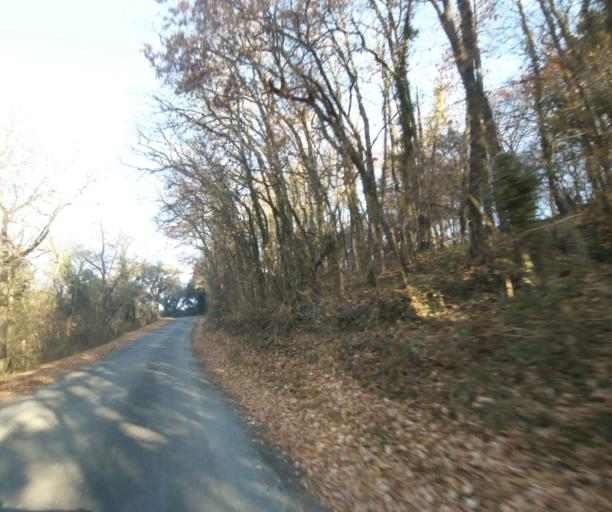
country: FR
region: Poitou-Charentes
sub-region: Departement de la Charente-Maritime
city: Fontcouverte
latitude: 45.7585
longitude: -0.6083
